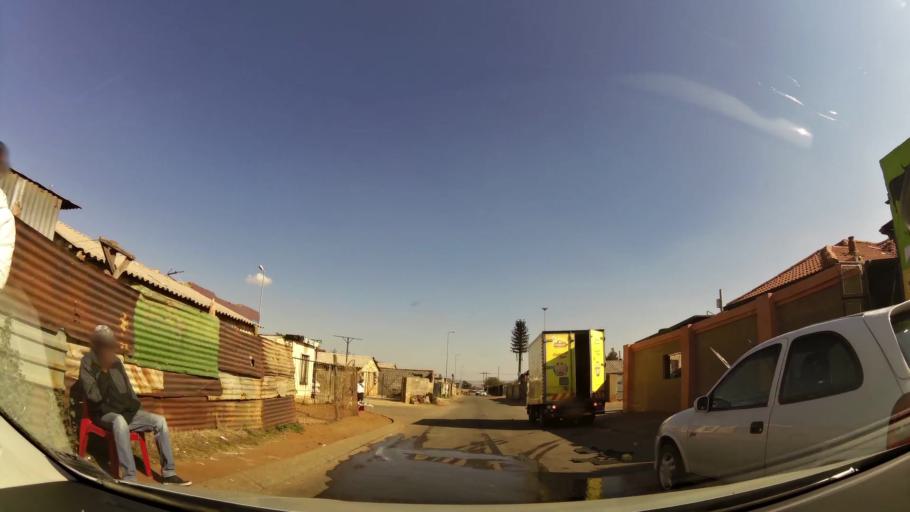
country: ZA
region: Gauteng
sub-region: City of Johannesburg Metropolitan Municipality
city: Soweto
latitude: -26.2857
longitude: 27.8681
